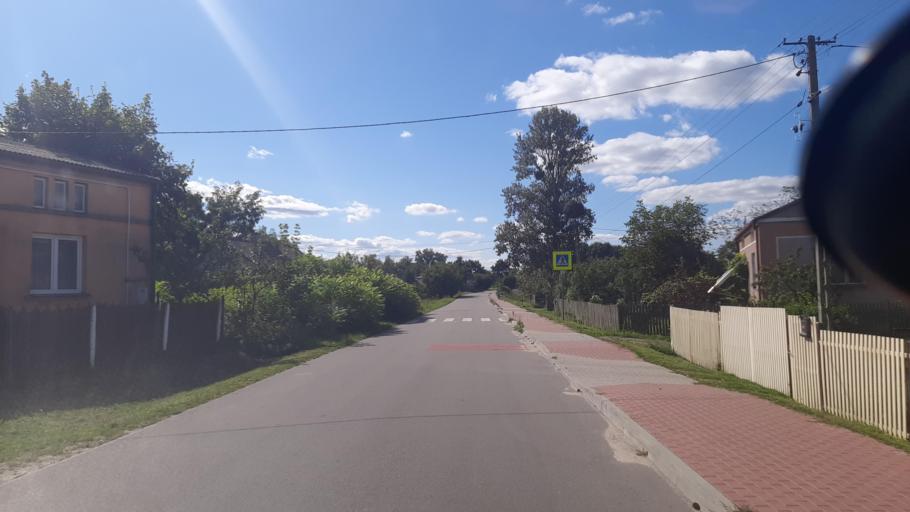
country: PL
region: Lublin Voivodeship
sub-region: Powiat lubelski
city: Garbow
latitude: 51.4026
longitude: 22.3381
